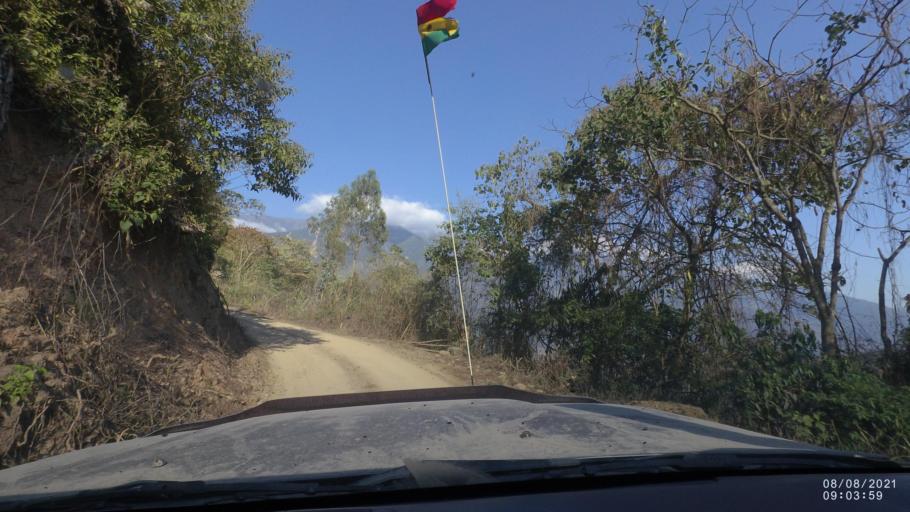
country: BO
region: La Paz
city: Quime
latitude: -16.5538
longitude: -66.7355
